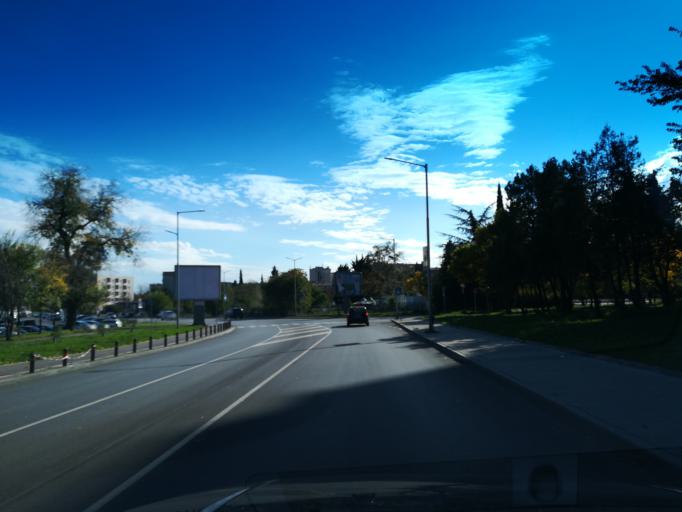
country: BG
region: Stara Zagora
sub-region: Obshtina Stara Zagora
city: Stara Zagora
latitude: 42.4331
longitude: 25.6373
